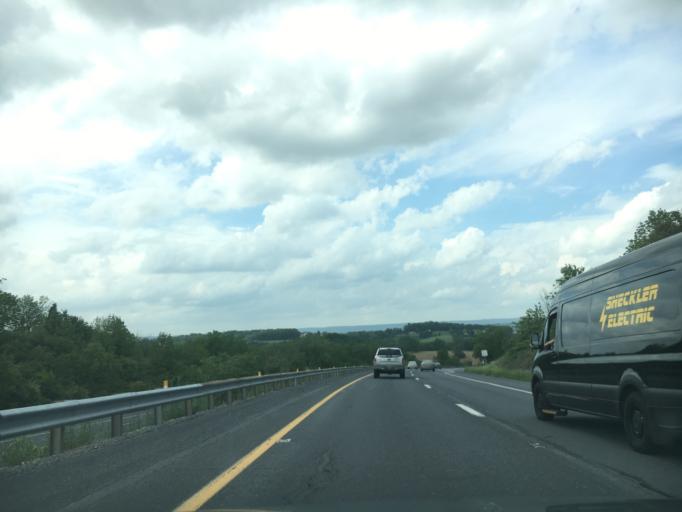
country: US
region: Pennsylvania
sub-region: Lehigh County
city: Egypt
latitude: 40.6871
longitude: -75.5233
